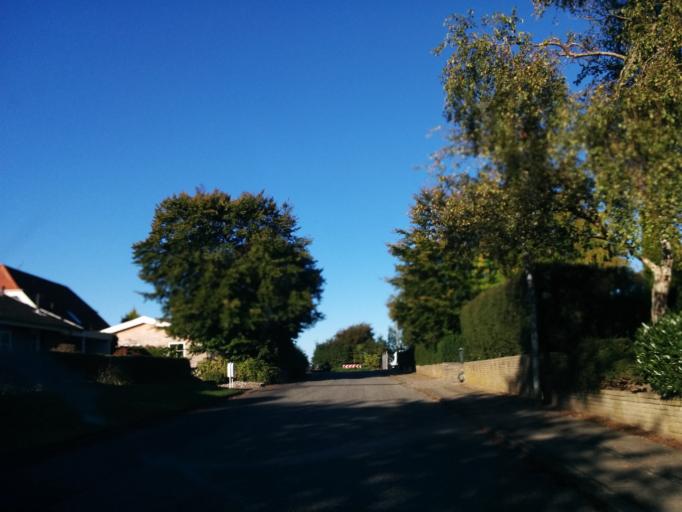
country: DK
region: South Denmark
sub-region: Kolding Kommune
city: Sonder Bjert
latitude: 55.4606
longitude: 9.5500
